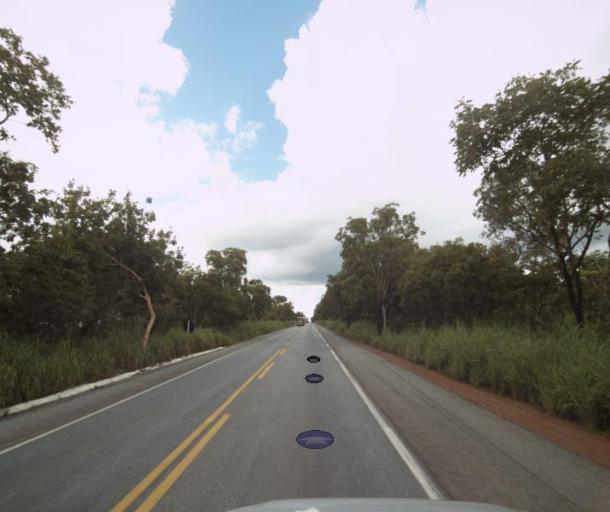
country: BR
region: Goias
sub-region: Porangatu
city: Porangatu
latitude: -13.2705
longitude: -49.1317
